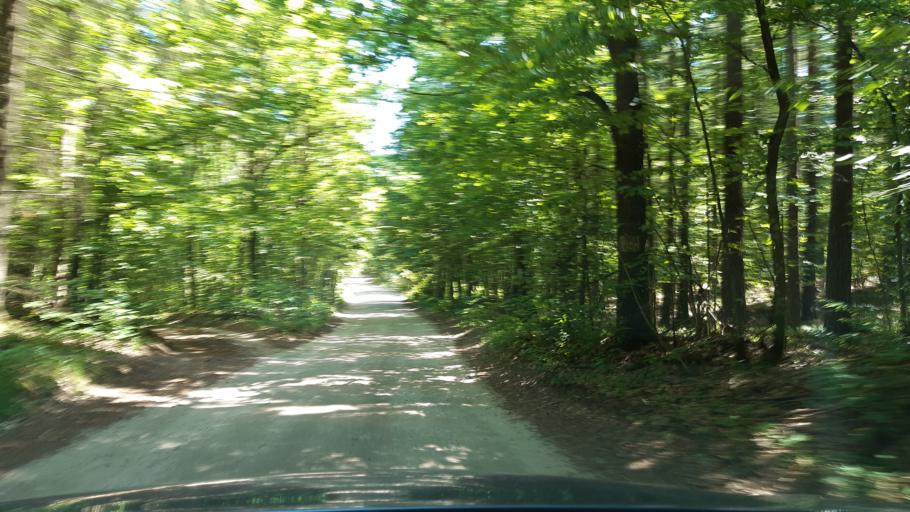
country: PL
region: Warmian-Masurian Voivodeship
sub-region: Powiat piski
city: Ruciane-Nida
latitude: 53.7127
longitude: 21.4941
